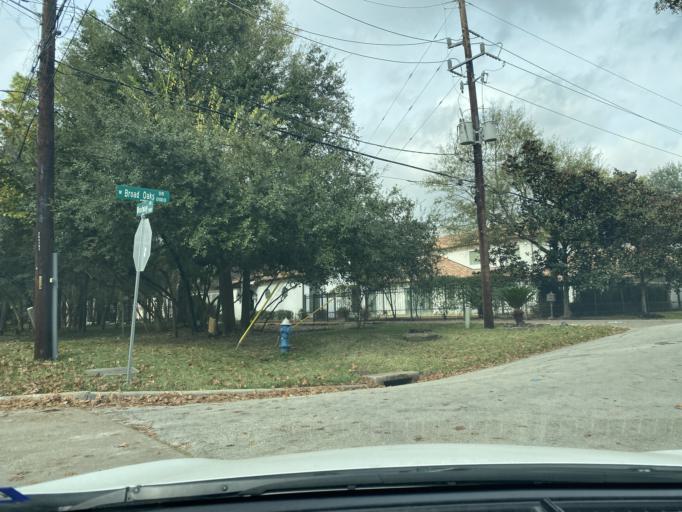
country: US
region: Texas
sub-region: Harris County
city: Hunters Creek Village
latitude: 29.7639
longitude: -95.4747
